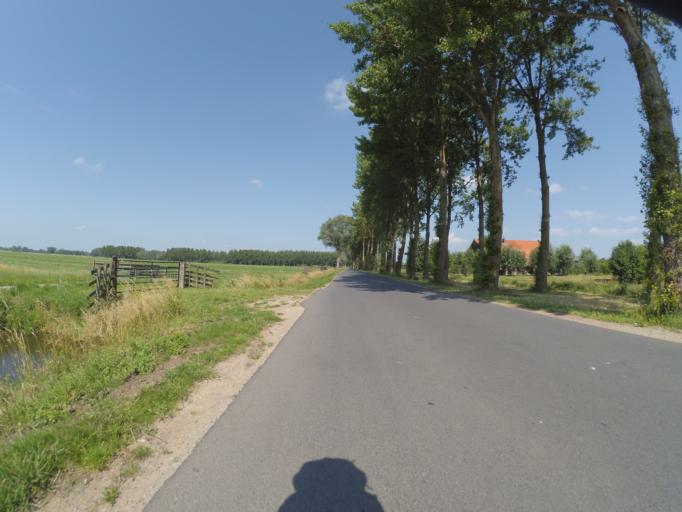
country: NL
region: South Holland
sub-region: Gemeente Leerdam
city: Leerdam
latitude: 51.9338
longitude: 5.1157
